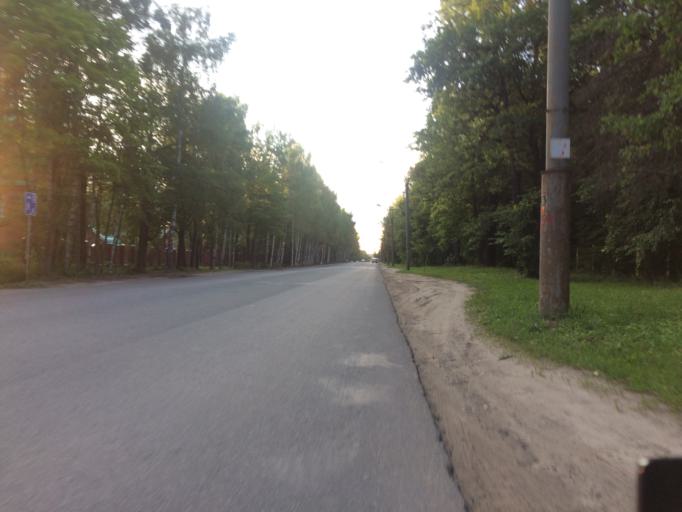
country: RU
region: Mariy-El
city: Yoshkar-Ola
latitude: 56.6222
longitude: 47.9552
